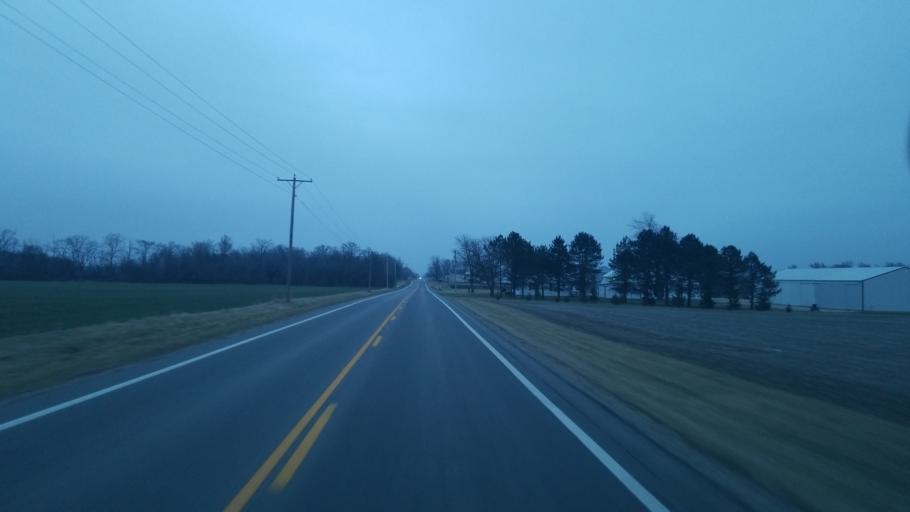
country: US
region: Ohio
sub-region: Mercer County
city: Rockford
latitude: 40.6550
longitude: -84.6296
